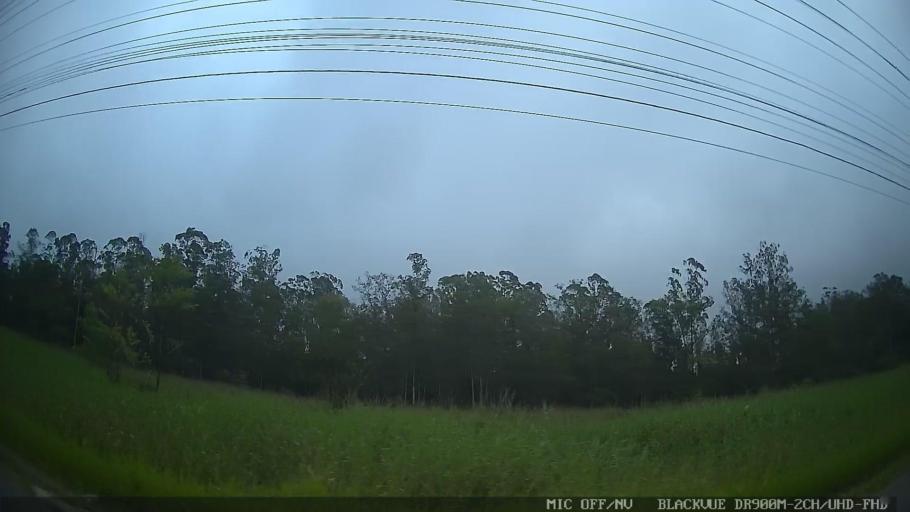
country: BR
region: Sao Paulo
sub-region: Mogi das Cruzes
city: Mogi das Cruzes
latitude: -23.5225
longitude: -46.1521
